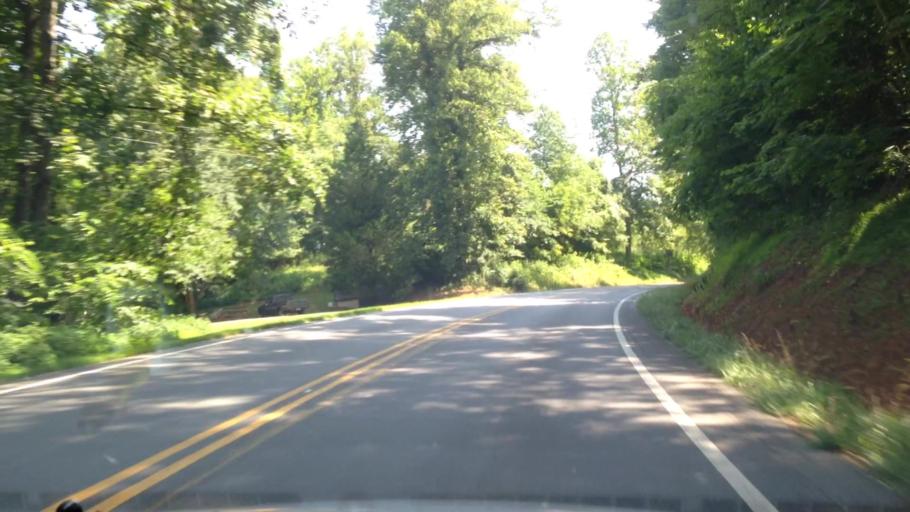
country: US
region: Virginia
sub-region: Patrick County
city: Stuart
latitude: 36.5886
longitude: -80.3298
